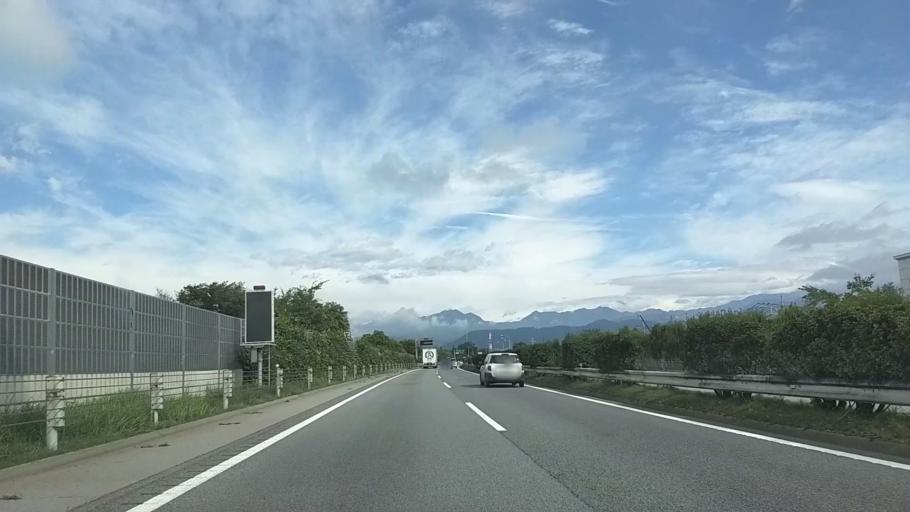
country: JP
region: Yamanashi
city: Ryuo
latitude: 35.6382
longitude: 138.5379
